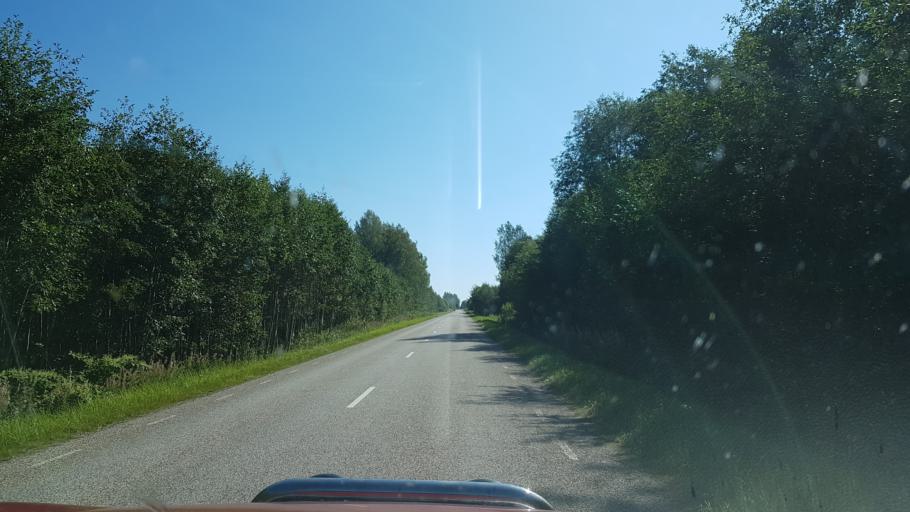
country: EE
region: Polvamaa
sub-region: Polva linn
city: Polva
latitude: 58.2458
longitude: 27.1944
